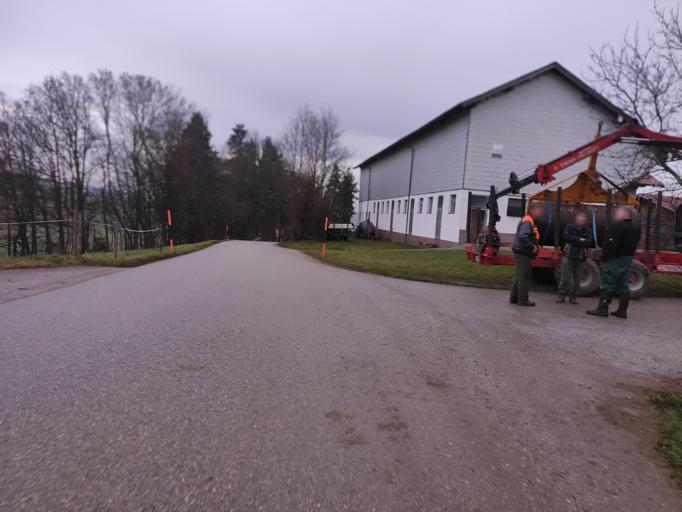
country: AT
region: Salzburg
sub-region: Politischer Bezirk Salzburg-Umgebung
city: Obertrum am See
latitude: 47.9218
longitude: 13.0727
